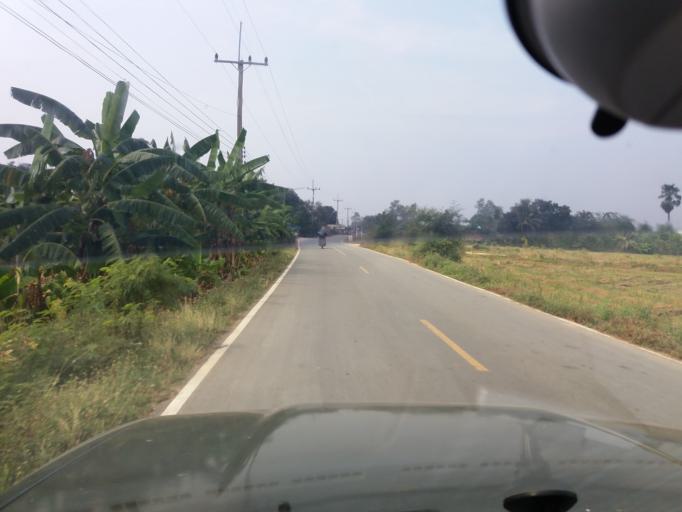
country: TH
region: Suphan Buri
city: Doem Bang Nang Buat
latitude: 14.8921
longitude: 100.1667
